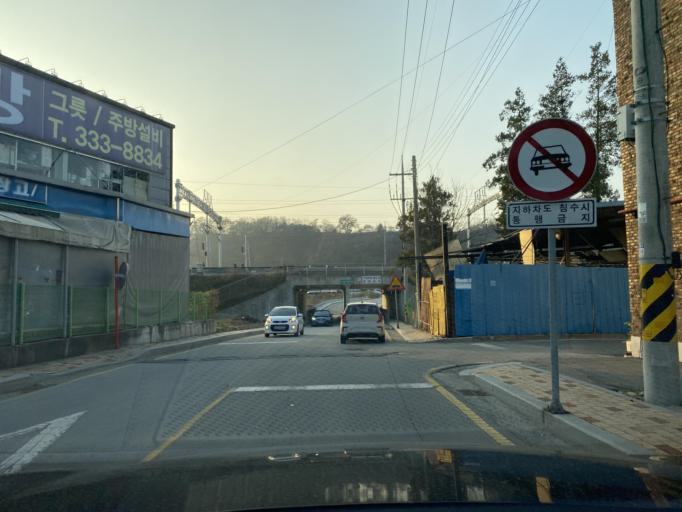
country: KR
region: Chungcheongnam-do
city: Yesan
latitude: 36.6906
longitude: 126.8296
